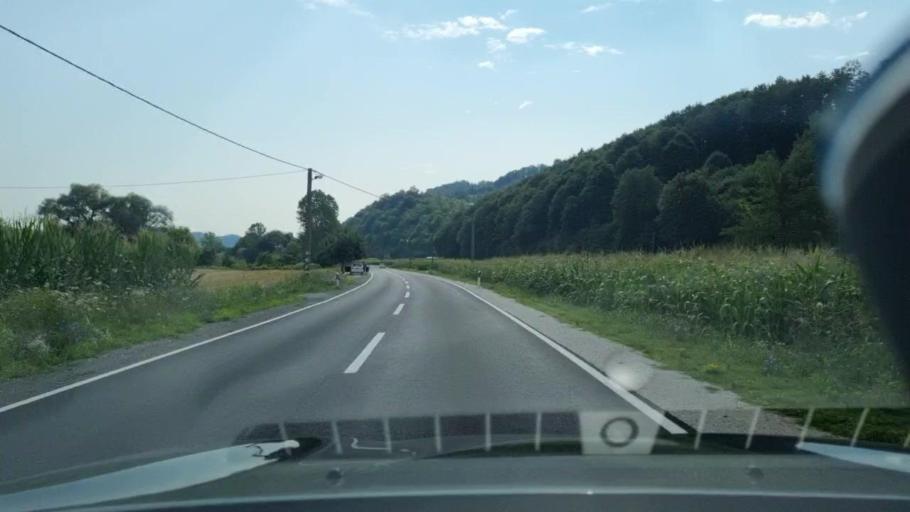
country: BA
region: Federation of Bosnia and Herzegovina
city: Otoka
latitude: 44.9809
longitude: 16.2023
